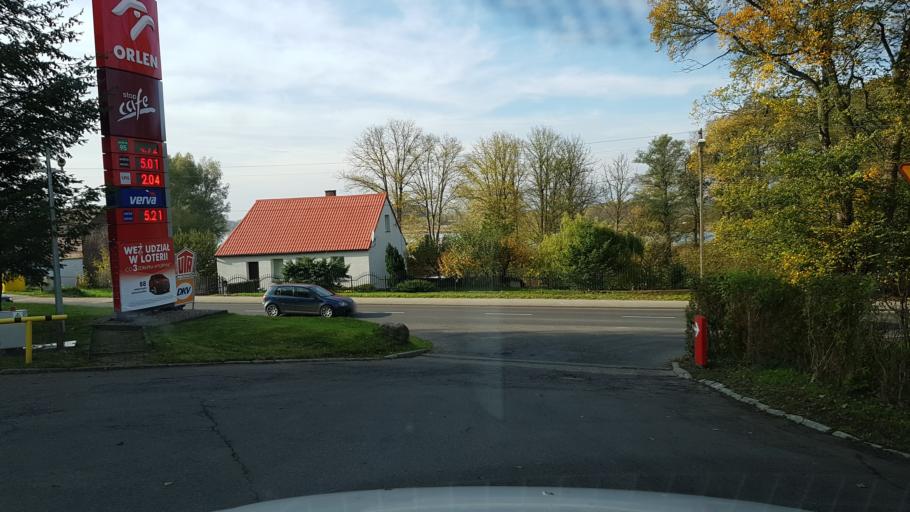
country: PL
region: West Pomeranian Voivodeship
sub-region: Powiat lobeski
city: Wegorzyno
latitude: 53.5346
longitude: 15.5571
